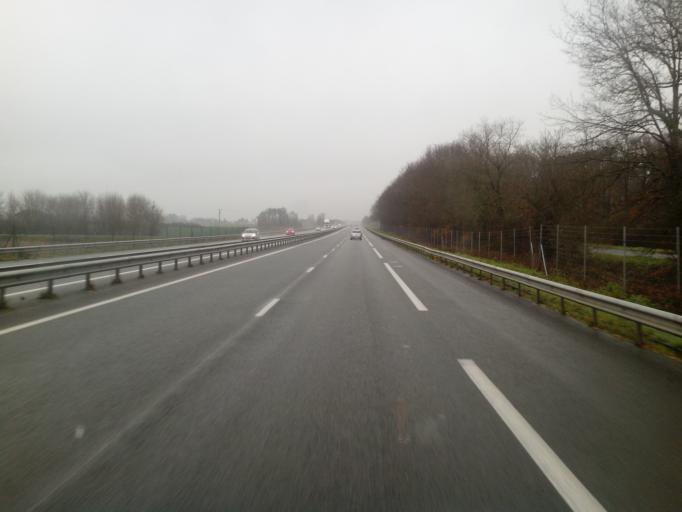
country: FR
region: Poitou-Charentes
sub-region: Departement de la Vienne
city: Savigny-Levescault
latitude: 46.4962
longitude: 0.4910
